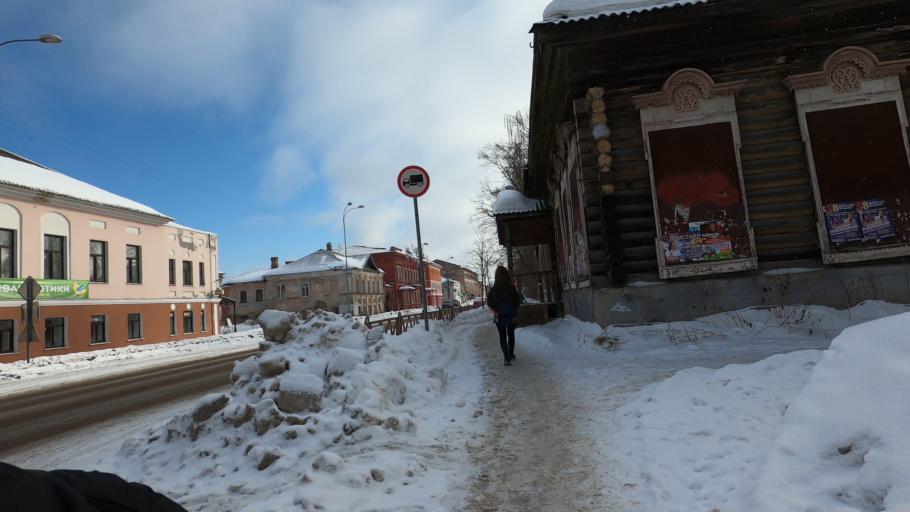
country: RU
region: Jaroslavl
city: Rybinsk
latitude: 58.0487
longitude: 38.8473
